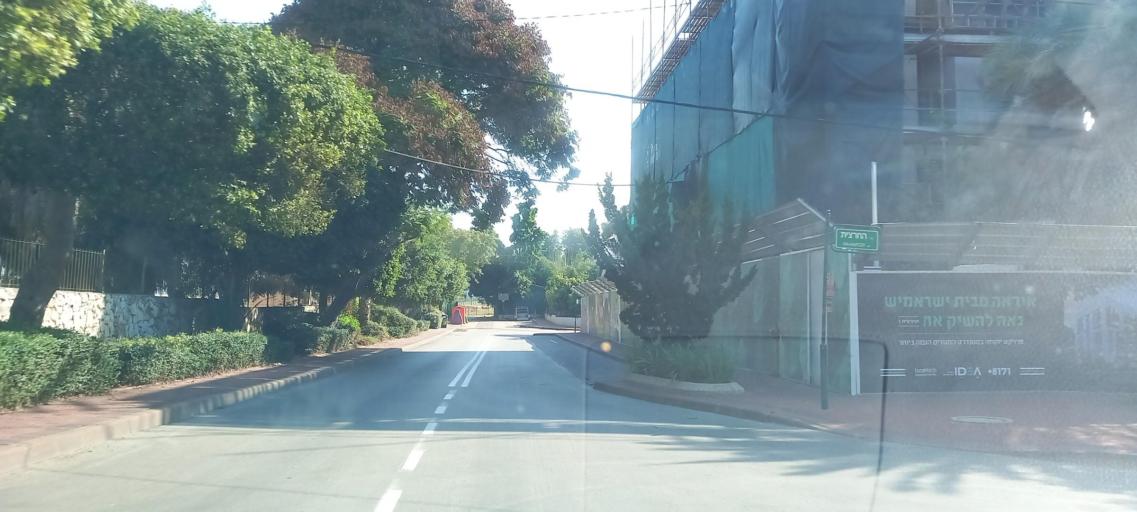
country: IL
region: Tel Aviv
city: Or Yehuda
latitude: 32.0476
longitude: 34.8378
